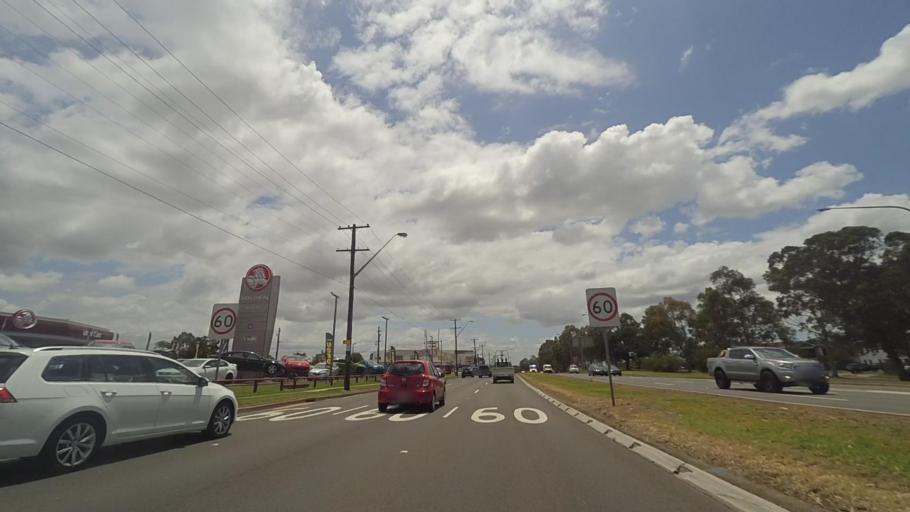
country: AU
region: New South Wales
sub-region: Campbelltown Municipality
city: Glenfield
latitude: -33.9373
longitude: 150.9140
